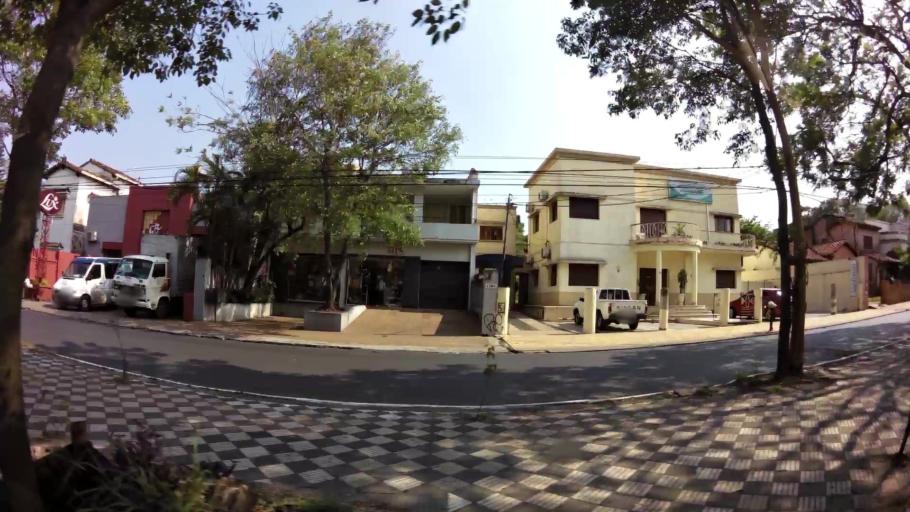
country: PY
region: Asuncion
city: Asuncion
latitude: -25.2893
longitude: -57.6575
